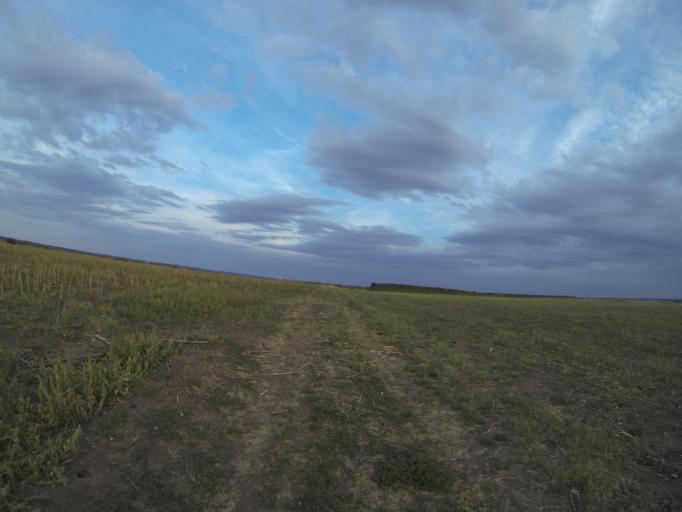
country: RO
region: Dolj
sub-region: Comuna Ceratu
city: Ceratu
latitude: 44.0958
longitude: 23.6674
